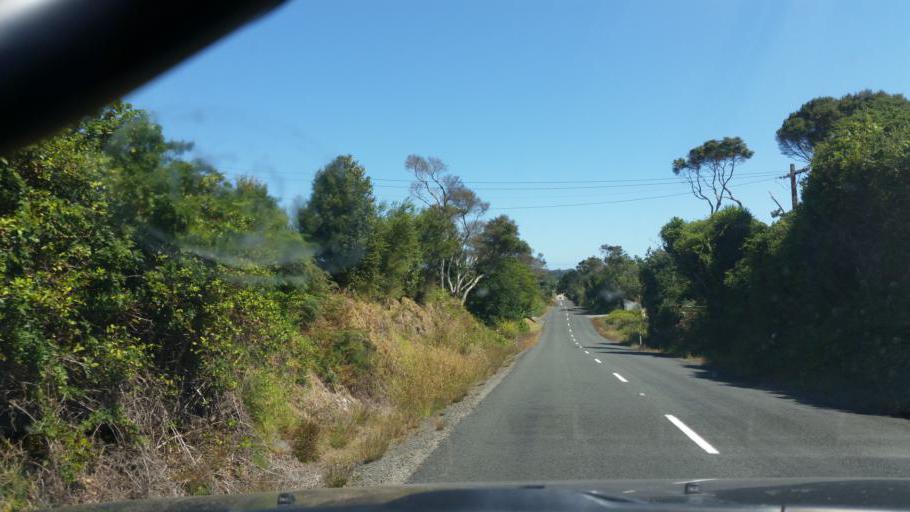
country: NZ
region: Northland
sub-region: Kaipara District
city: Dargaville
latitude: -36.0120
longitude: 173.9375
